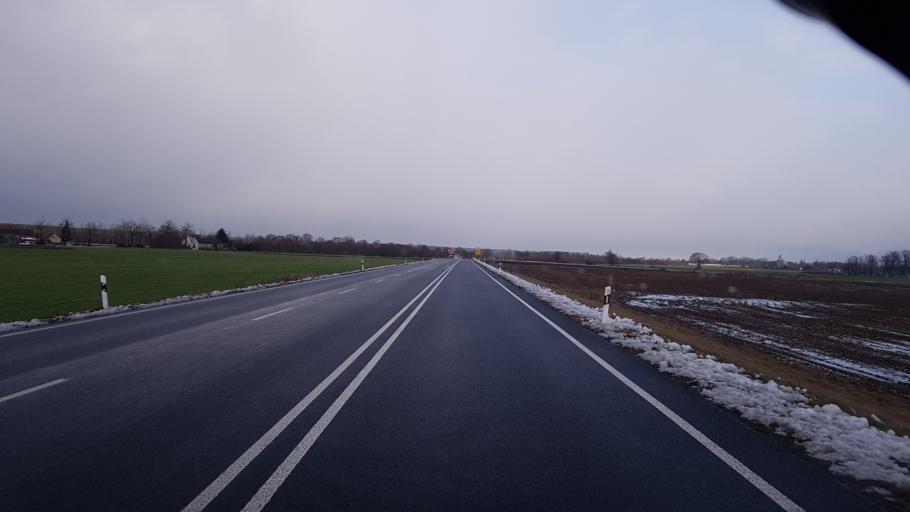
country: DE
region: Brandenburg
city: Schenkendobern
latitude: 51.8726
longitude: 14.6252
